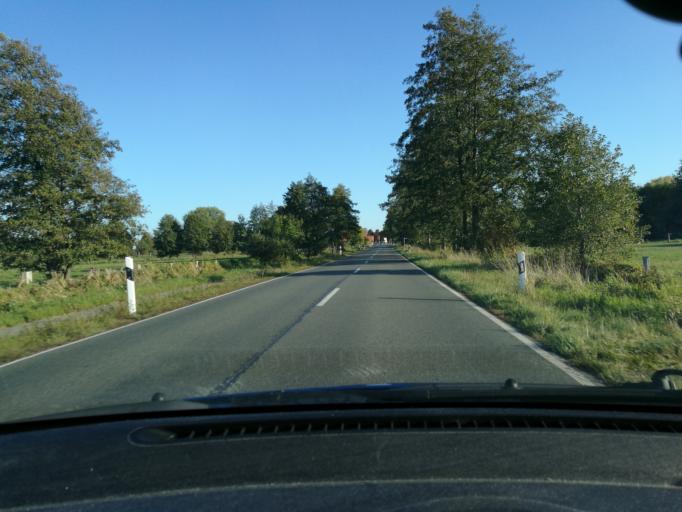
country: DE
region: Lower Saxony
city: Bleckede
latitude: 53.3005
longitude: 10.7103
